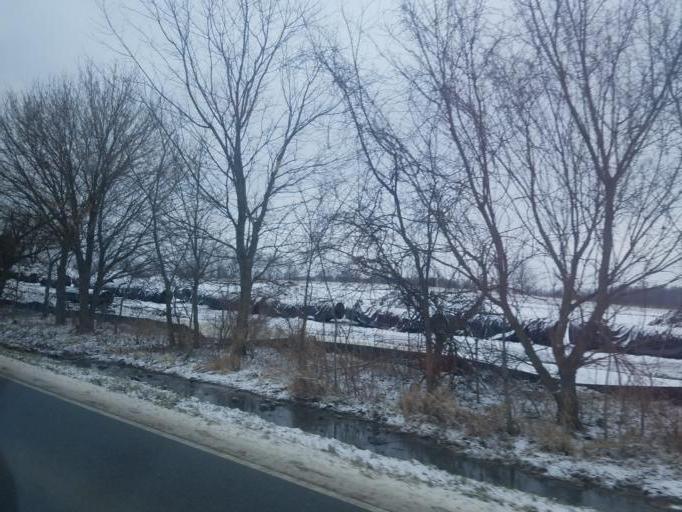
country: US
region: Ohio
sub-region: Franklin County
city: New Albany
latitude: 40.0506
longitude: -82.7593
